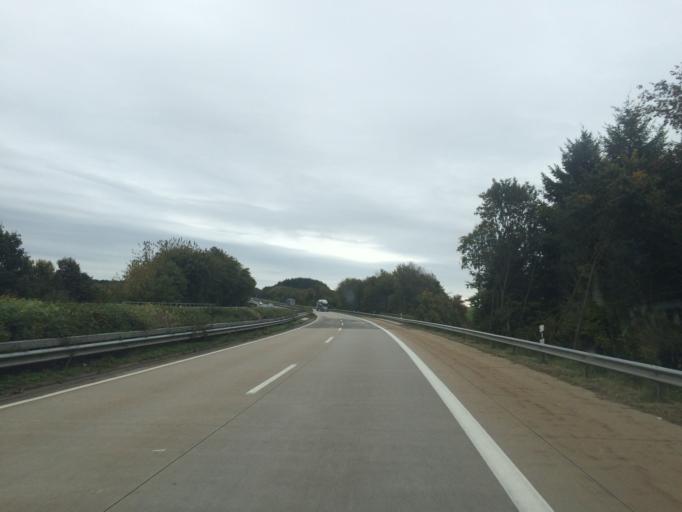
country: DE
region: Rheinland-Pfalz
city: Eckfeld
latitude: 50.1135
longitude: 6.8526
